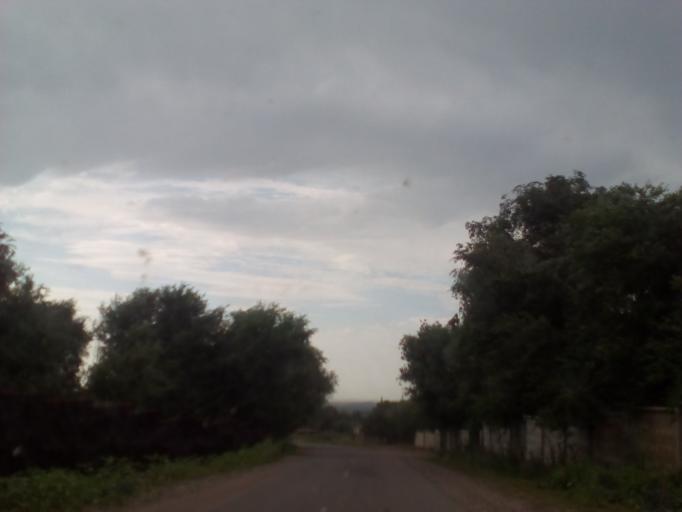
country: KZ
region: Almaty Oblysy
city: Burunday
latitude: 43.1565
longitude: 76.3845
